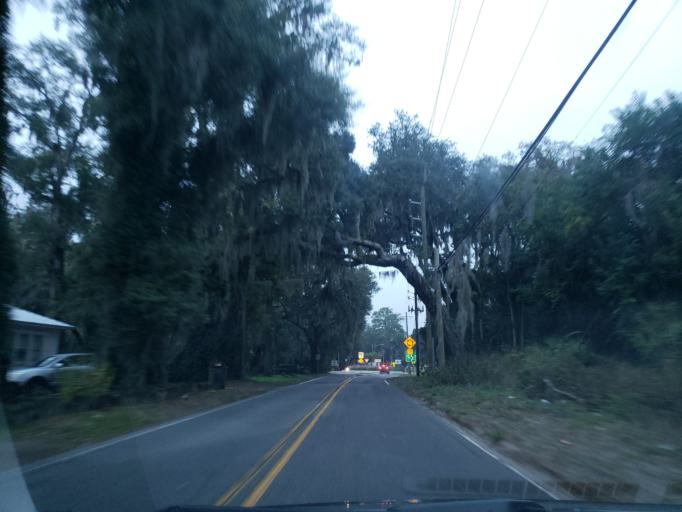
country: US
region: Georgia
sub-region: Chatham County
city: Thunderbolt
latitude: 32.0141
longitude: -81.0656
